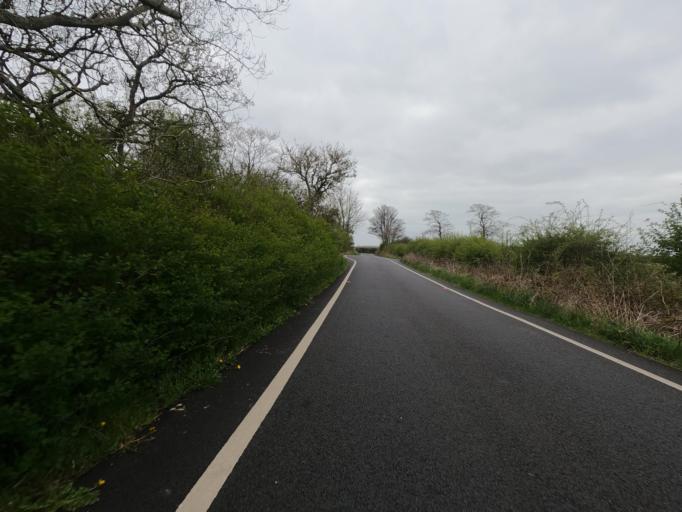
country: GB
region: England
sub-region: Newcastle upon Tyne
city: Dinnington
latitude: 55.0574
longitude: -1.6872
